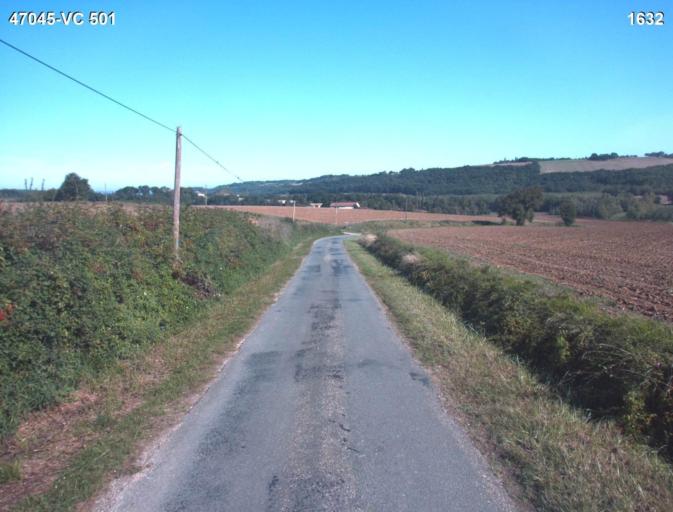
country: FR
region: Aquitaine
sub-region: Departement du Lot-et-Garonne
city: Nerac
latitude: 44.1630
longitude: 0.4146
